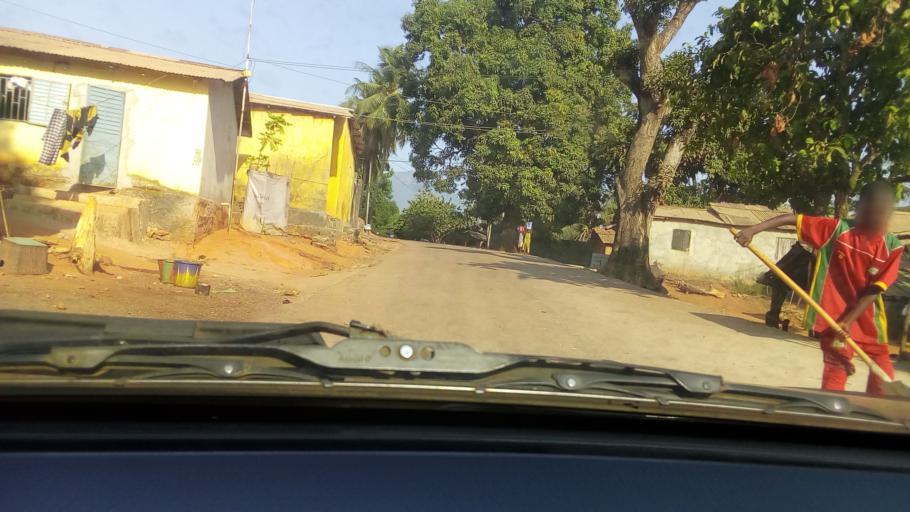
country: GN
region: Kindia
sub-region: Prefecture de Dubreka
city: Dubreka
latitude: 9.7877
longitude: -13.5265
